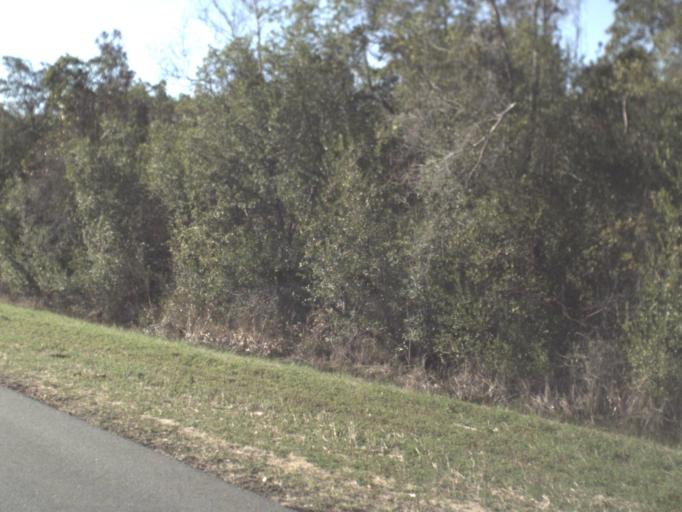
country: US
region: Florida
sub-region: Bay County
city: Youngstown
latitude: 30.4352
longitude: -85.3659
